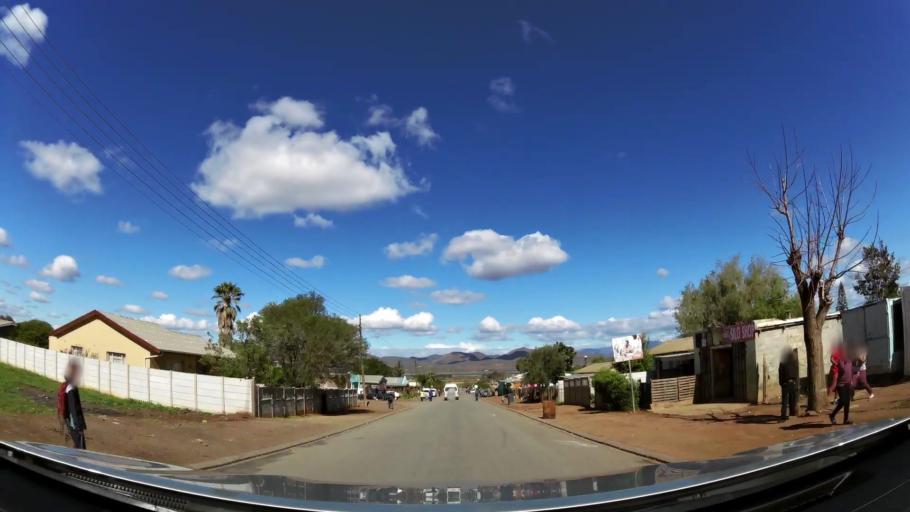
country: ZA
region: Western Cape
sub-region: Cape Winelands District Municipality
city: Ashton
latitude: -33.8323
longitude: 20.0433
